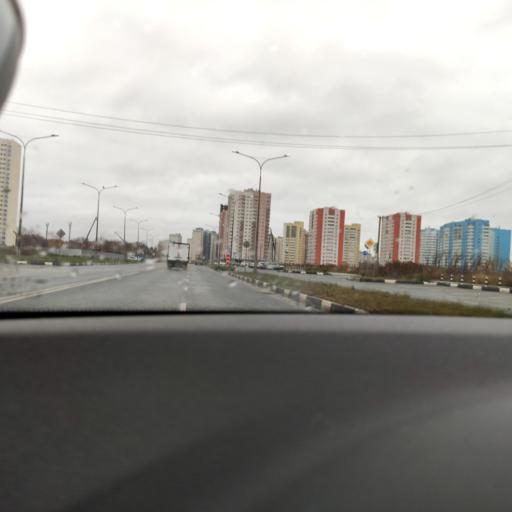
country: RU
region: Samara
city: Samara
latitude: 53.1427
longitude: 50.0776
